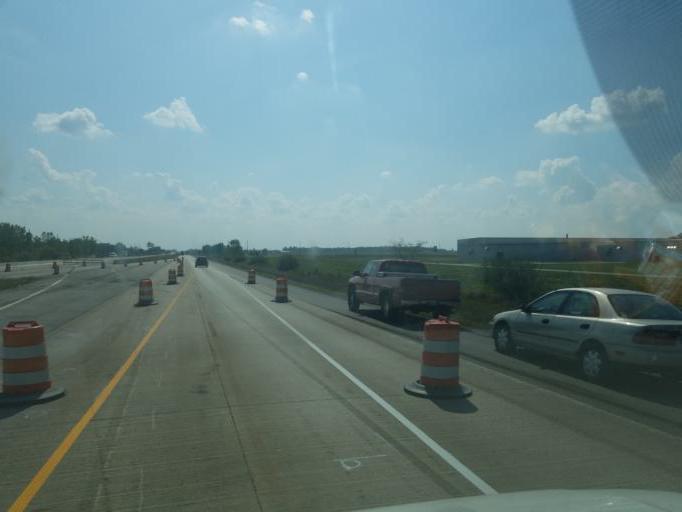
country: US
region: Indiana
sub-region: DeKalb County
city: Auburn
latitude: 41.3500
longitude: -85.0880
